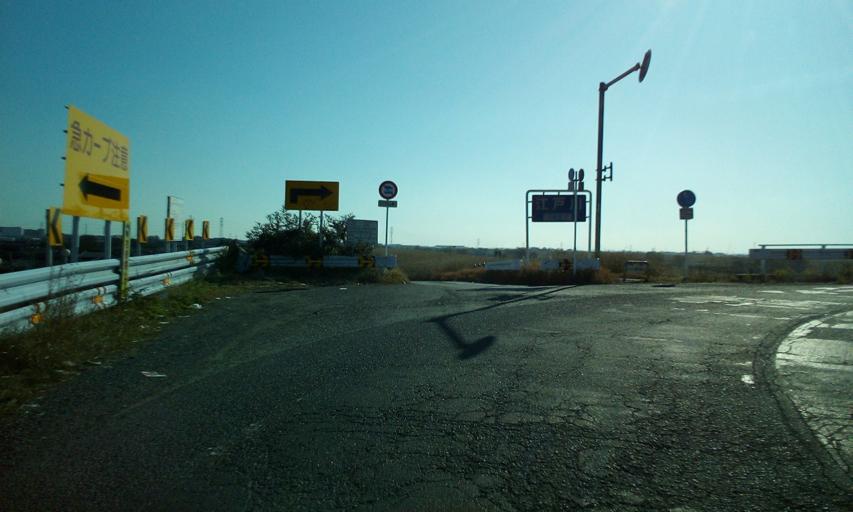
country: JP
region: Ibaraki
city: Sakai
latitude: 36.0821
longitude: 139.7826
